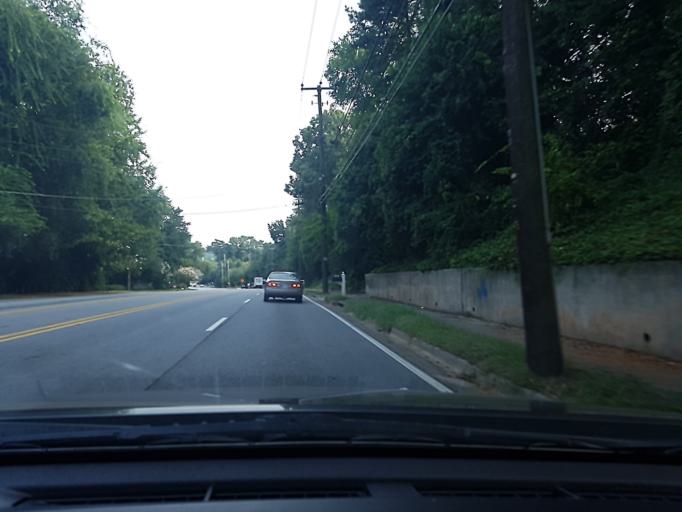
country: US
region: Georgia
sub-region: DeKalb County
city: North Atlanta
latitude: 33.8375
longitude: -84.3433
